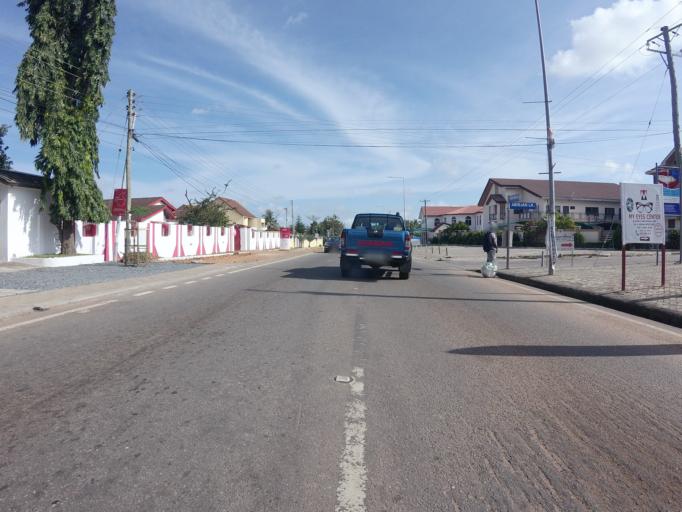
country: GH
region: Greater Accra
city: Medina Estates
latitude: 5.6379
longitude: -0.1617
